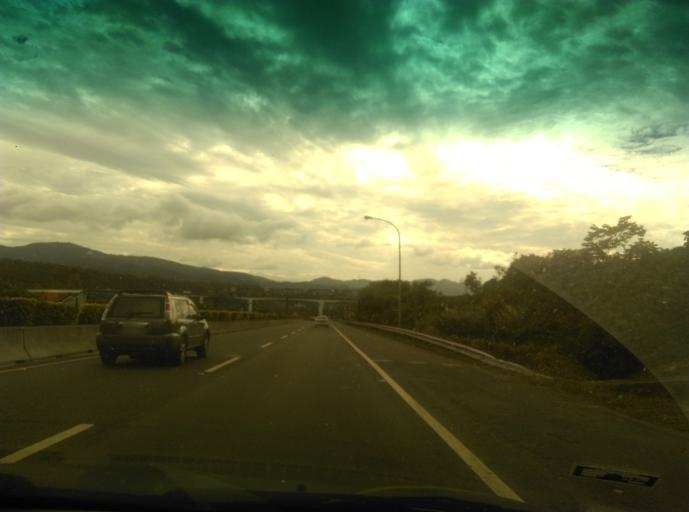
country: TW
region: Taiwan
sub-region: Keelung
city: Keelung
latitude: 25.1107
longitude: 121.7264
